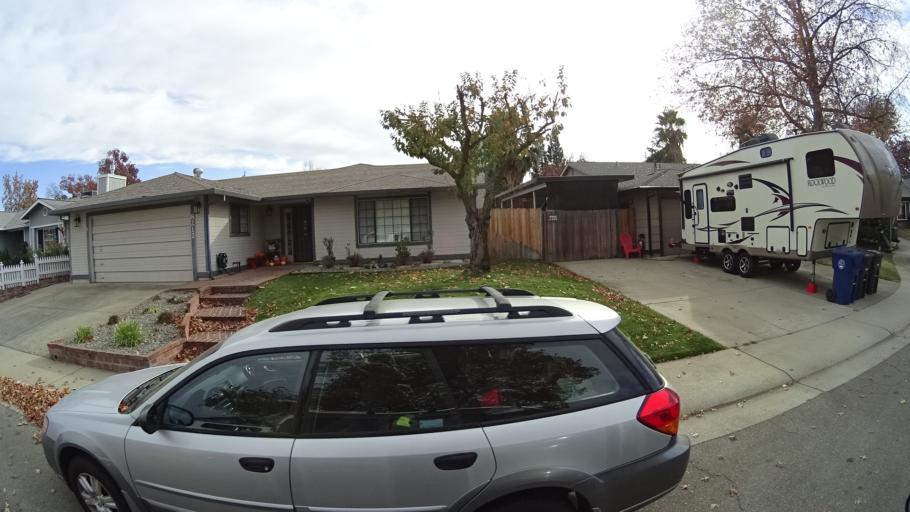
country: US
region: California
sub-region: Sacramento County
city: Citrus Heights
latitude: 38.7065
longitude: -121.2556
